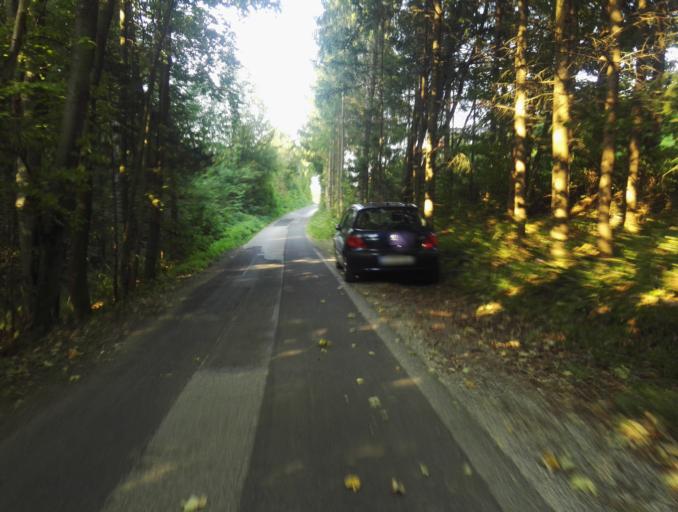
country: AT
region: Styria
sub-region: Politischer Bezirk Graz-Umgebung
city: Sankt Oswald bei Plankenwarth
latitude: 47.0943
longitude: 15.2855
